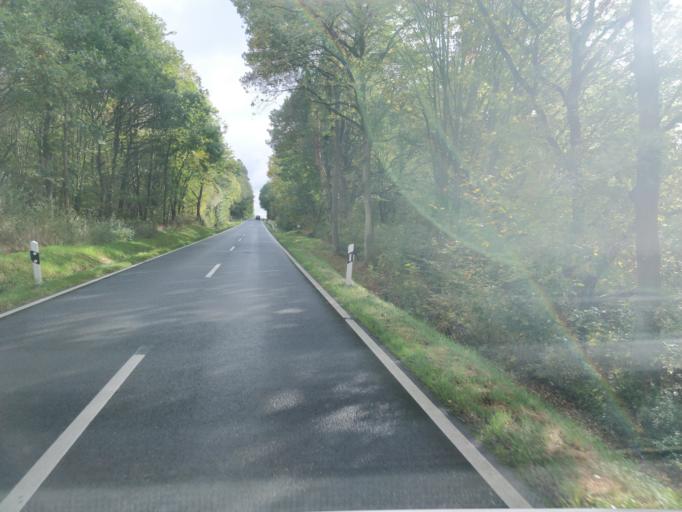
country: DE
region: Hesse
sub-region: Regierungsbezirk Darmstadt
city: Neu-Anspach
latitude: 50.3395
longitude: 8.5078
